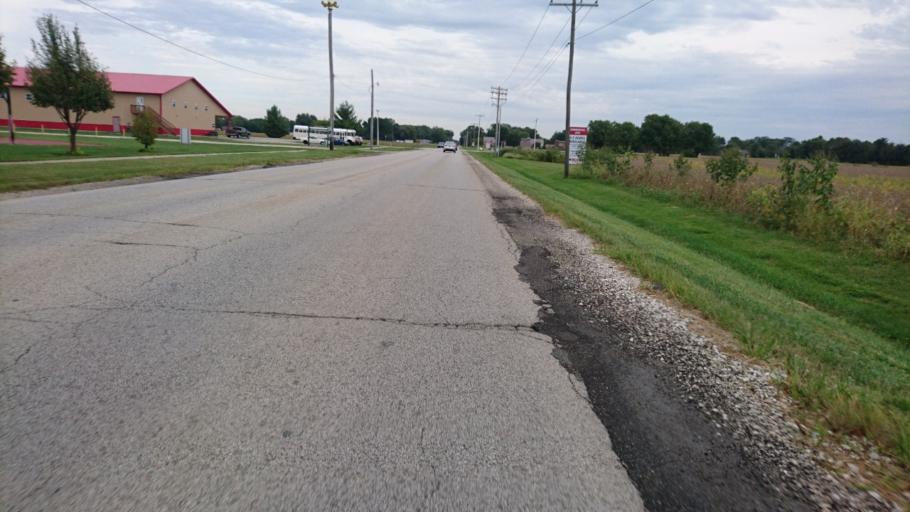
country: US
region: Illinois
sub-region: Sangamon County
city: Chatham
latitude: 39.6767
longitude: -89.6927
